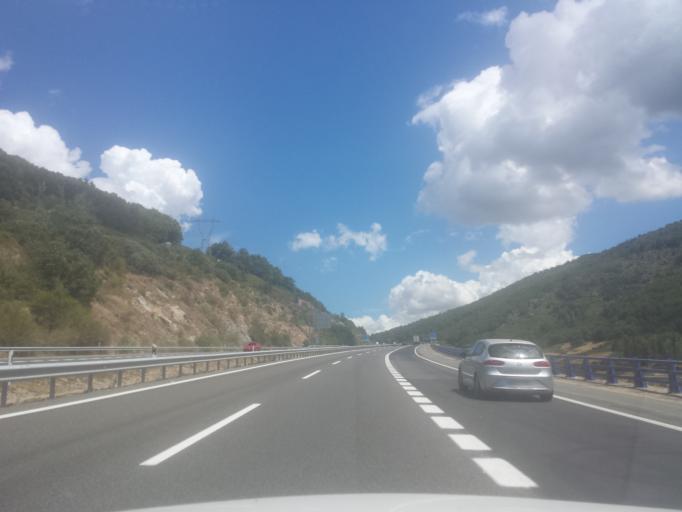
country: ES
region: Extremadura
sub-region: Provincia de Caceres
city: Banos de Montemayor
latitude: 40.3268
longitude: -5.8606
